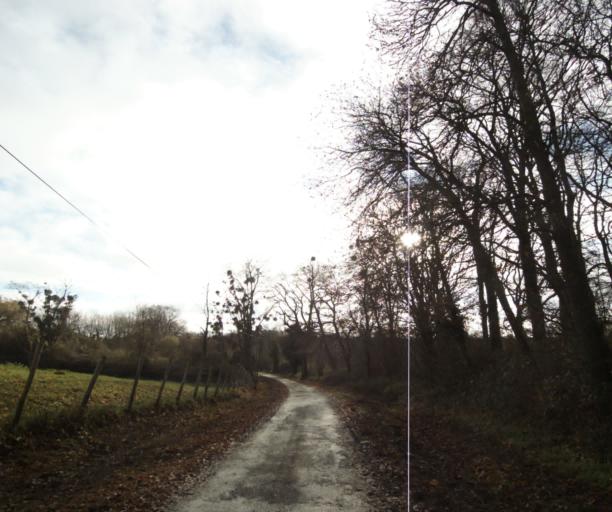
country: FR
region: Pays de la Loire
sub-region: Departement de la Sarthe
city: La Chapelle-Saint-Aubin
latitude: 48.0244
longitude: 0.1637
